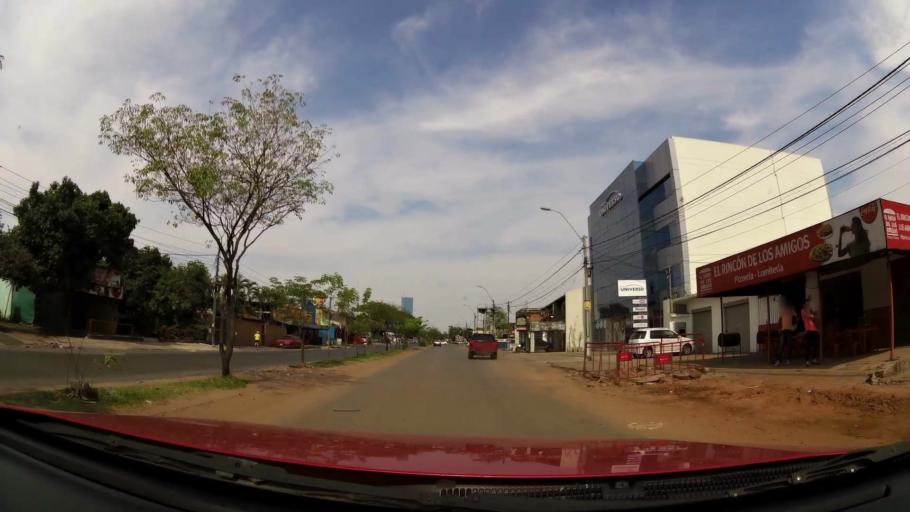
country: PY
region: Central
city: Fernando de la Mora
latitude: -25.2760
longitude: -57.5477
